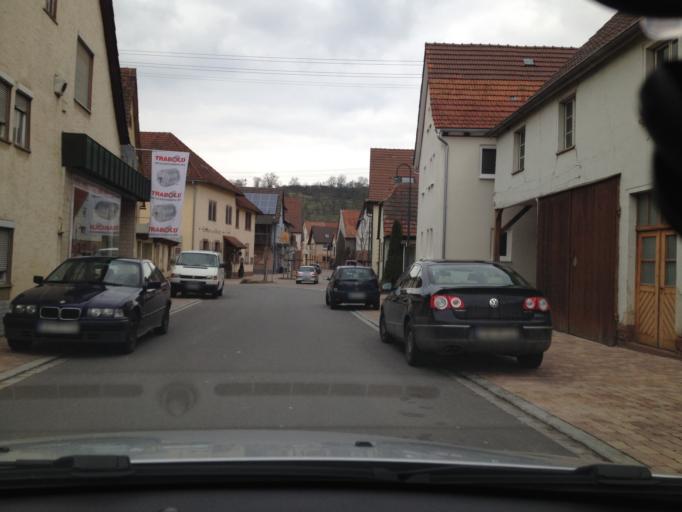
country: DE
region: Baden-Wuerttemberg
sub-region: Regierungsbezirk Stuttgart
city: Wertheim
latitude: 49.7259
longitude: 9.5335
